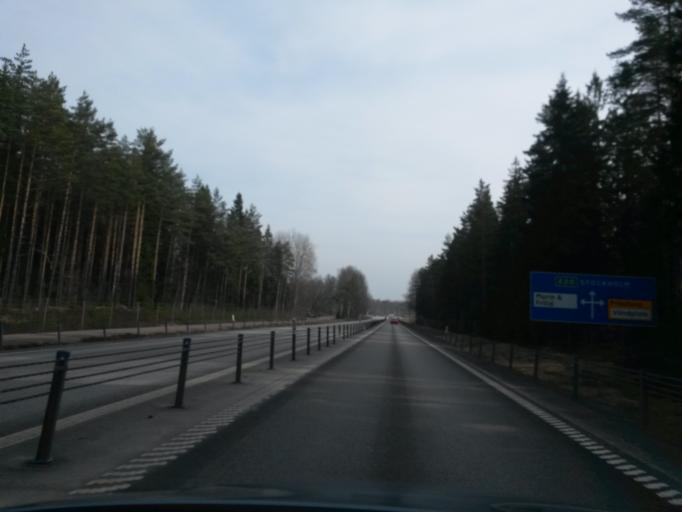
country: SE
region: OErebro
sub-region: Laxa Kommun
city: Laxa
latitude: 58.9761
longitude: 14.5855
